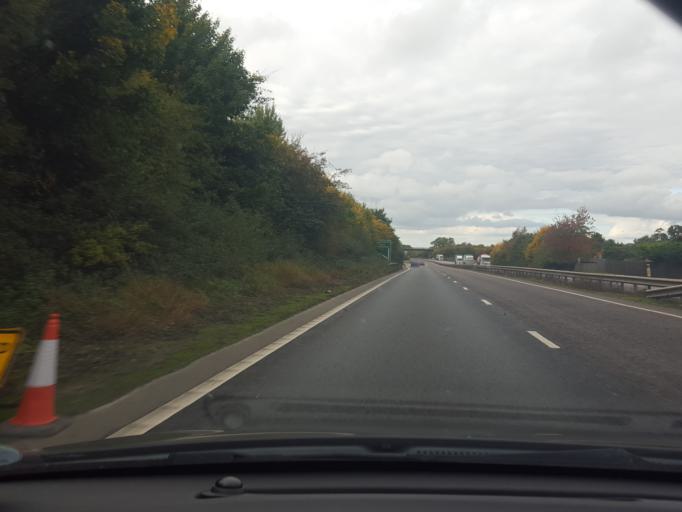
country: GB
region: England
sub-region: Suffolk
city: Woolpit
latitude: 52.2284
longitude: 0.8975
